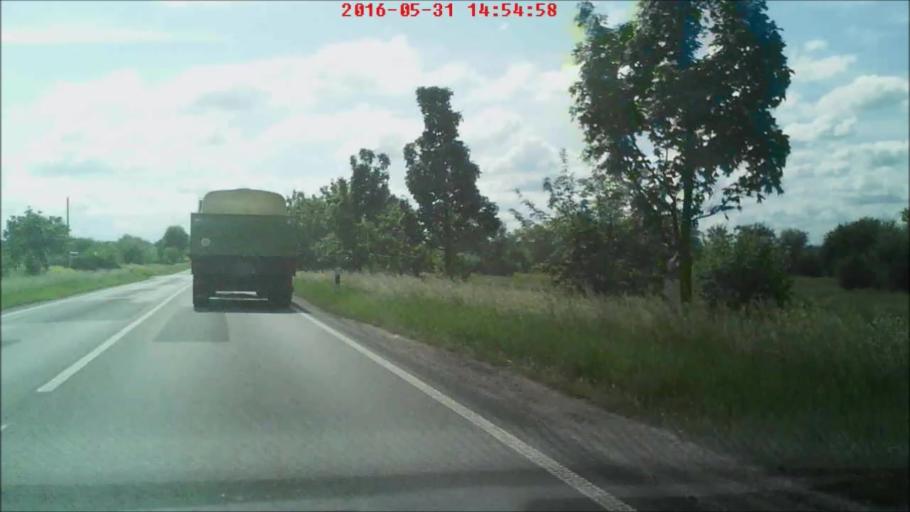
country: DE
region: Thuringia
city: Weissensee
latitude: 51.1888
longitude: 11.0582
